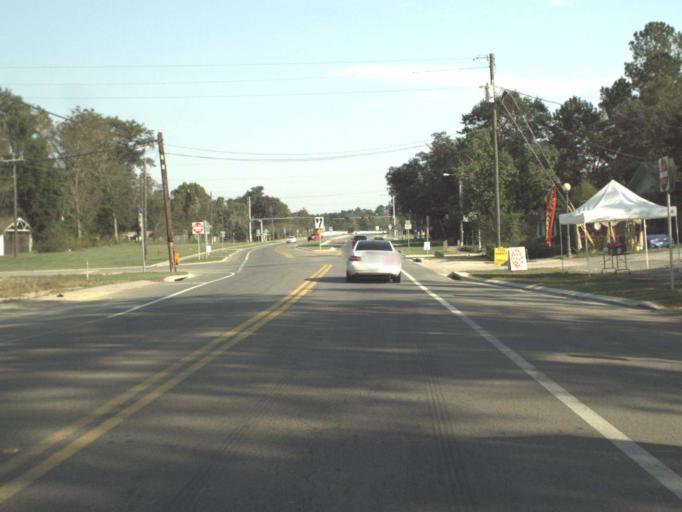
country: US
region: Florida
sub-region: Holmes County
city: Bonifay
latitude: 30.6224
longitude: -85.7123
